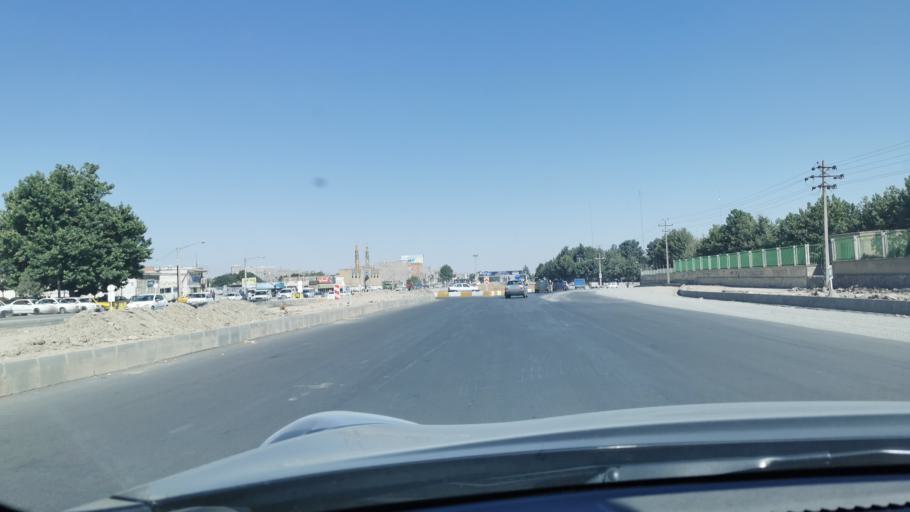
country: IR
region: Razavi Khorasan
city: Chenaran
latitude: 36.6396
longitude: 59.1203
